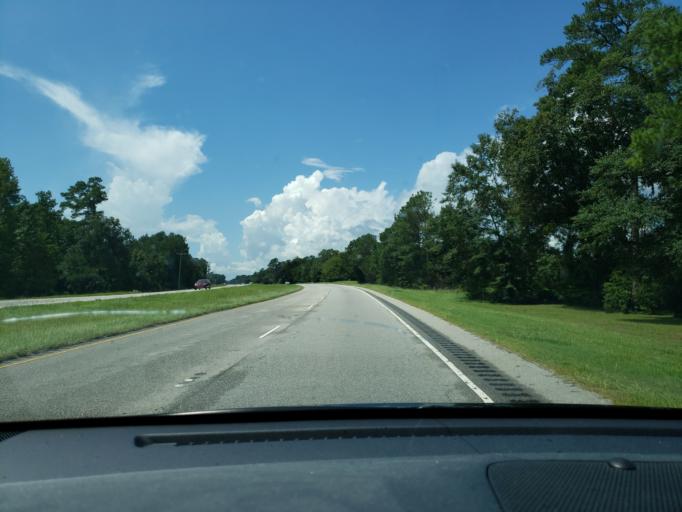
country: US
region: North Carolina
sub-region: Bladen County
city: Elizabethtown
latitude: 34.6452
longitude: -78.6871
